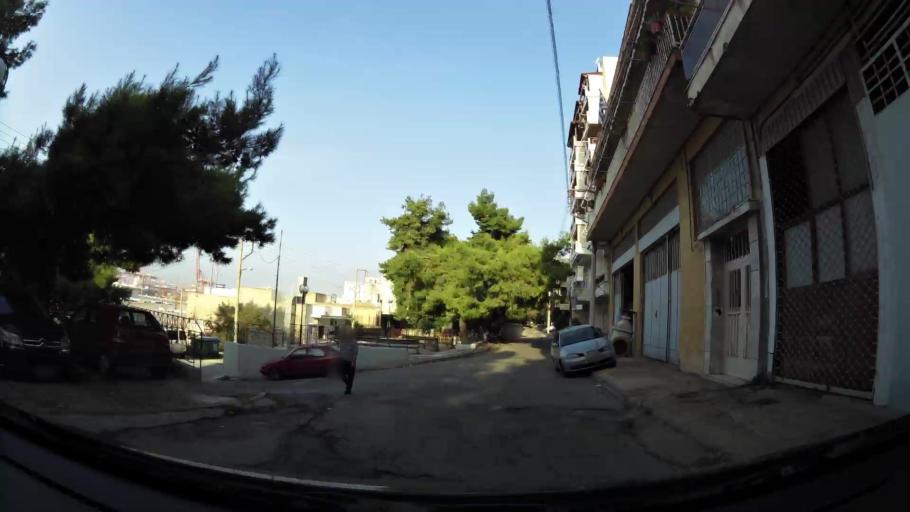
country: GR
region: Attica
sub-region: Nomos Piraios
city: Keratsini
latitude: 37.9605
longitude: 23.6137
